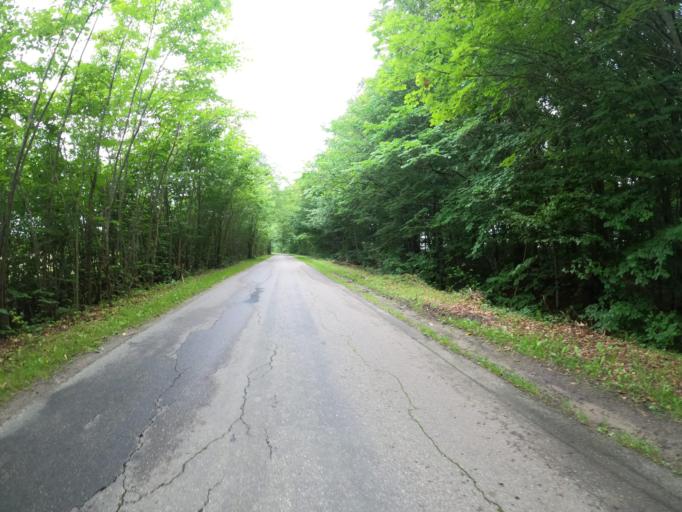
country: PL
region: West Pomeranian Voivodeship
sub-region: Powiat szczecinecki
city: Grzmiaca
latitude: 53.9378
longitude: 16.4558
